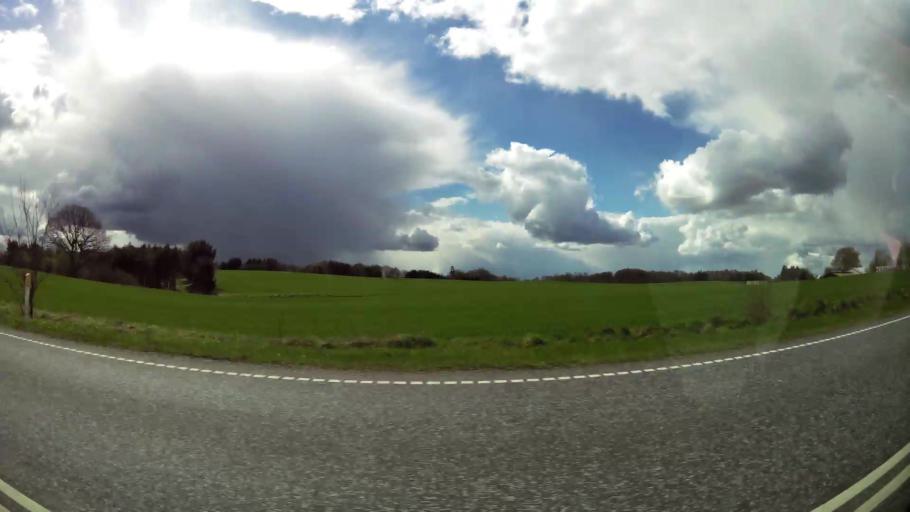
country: DK
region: South Denmark
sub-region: Vejle Kommune
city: Jelling
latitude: 55.6953
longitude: 9.3857
